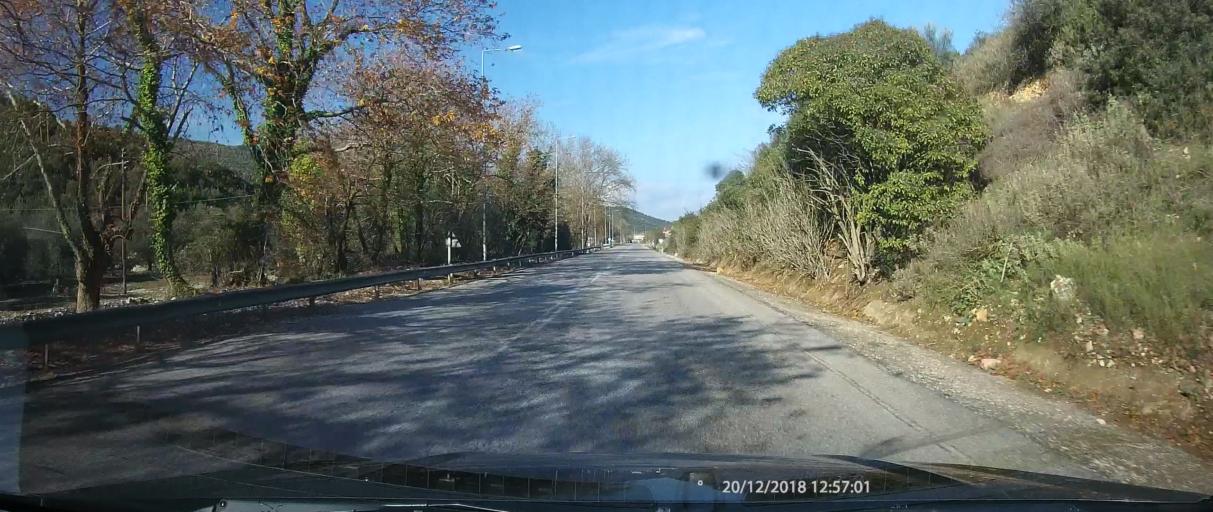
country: GR
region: West Greece
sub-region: Nomos Aitolias kai Akarnanias
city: Pappadhatai
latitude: 38.5178
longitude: 21.3803
